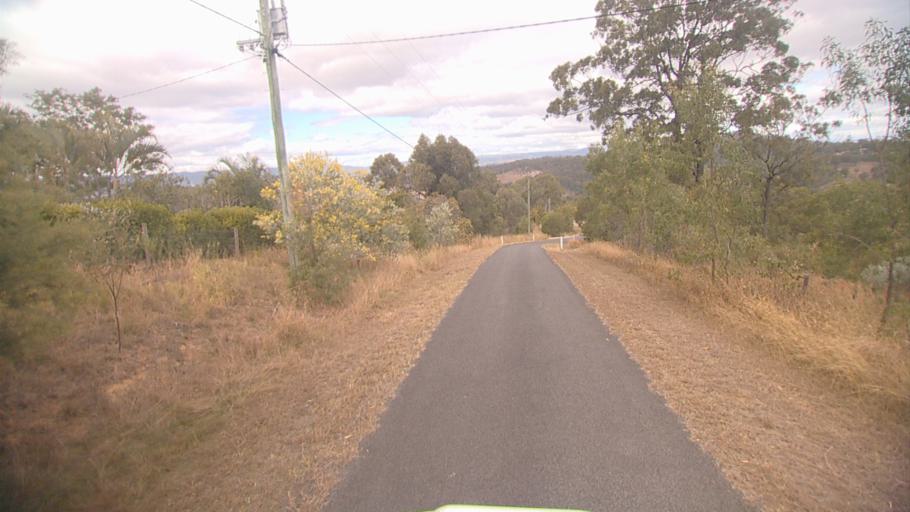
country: AU
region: Queensland
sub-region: Logan
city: Cedar Vale
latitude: -27.9005
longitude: 153.0379
